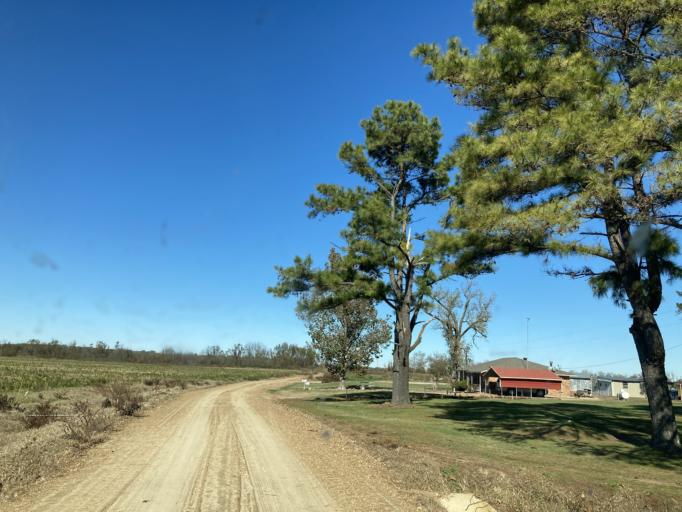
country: US
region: Mississippi
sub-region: Hinds County
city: Lynchburg
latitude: 32.6296
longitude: -90.5755
